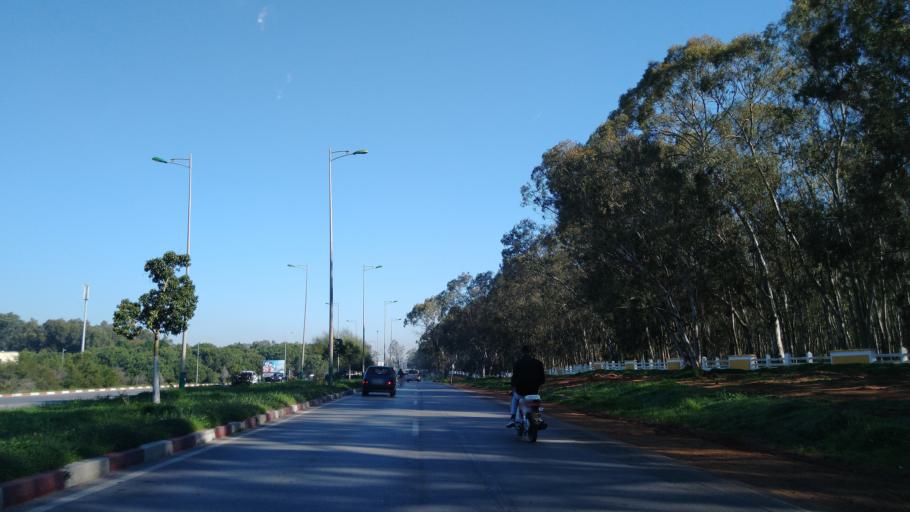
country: MA
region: Rabat-Sale-Zemmour-Zaer
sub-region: Skhirate-Temara
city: Temara
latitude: 33.9384
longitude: -6.8811
